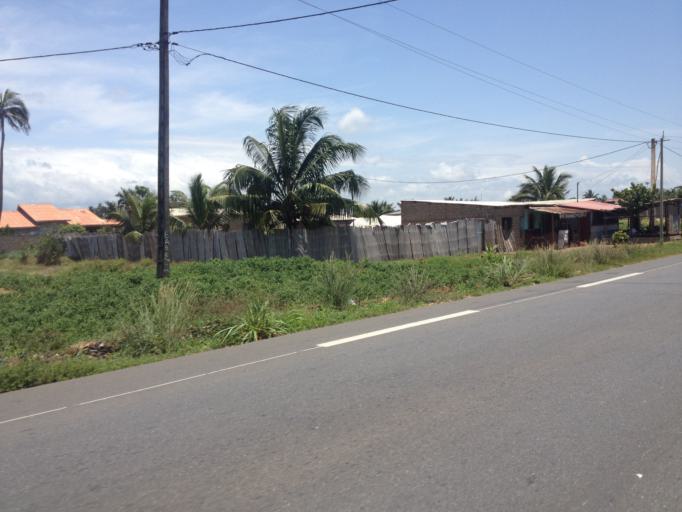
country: BJ
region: Mono
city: Grand-Popo
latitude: 6.2698
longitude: 1.7822
